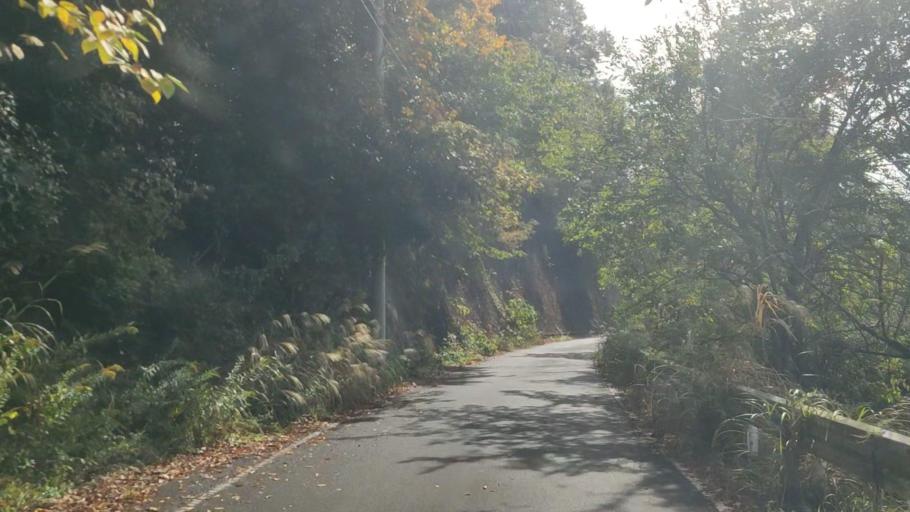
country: JP
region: Yamanashi
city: Ryuo
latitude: 35.4557
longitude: 138.4488
